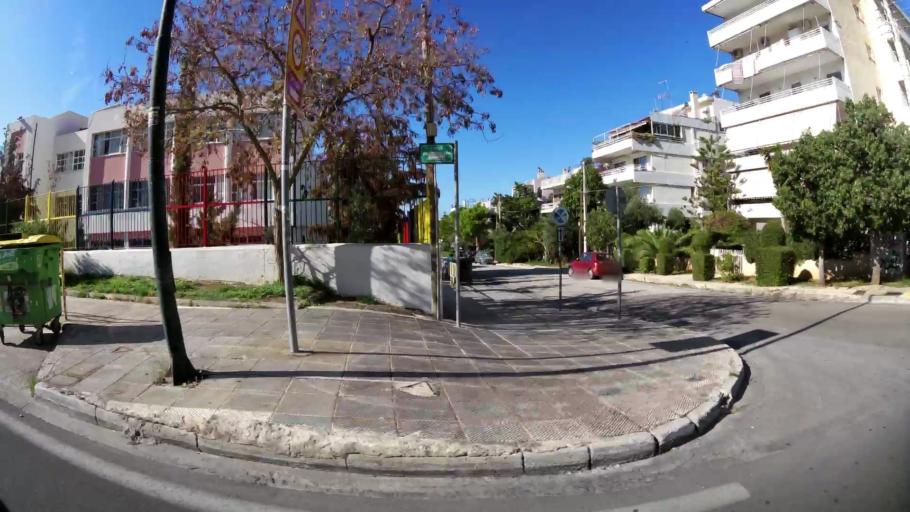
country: GR
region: Attica
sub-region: Nomarchia Athinas
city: Glyfada
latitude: 37.8673
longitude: 23.7675
